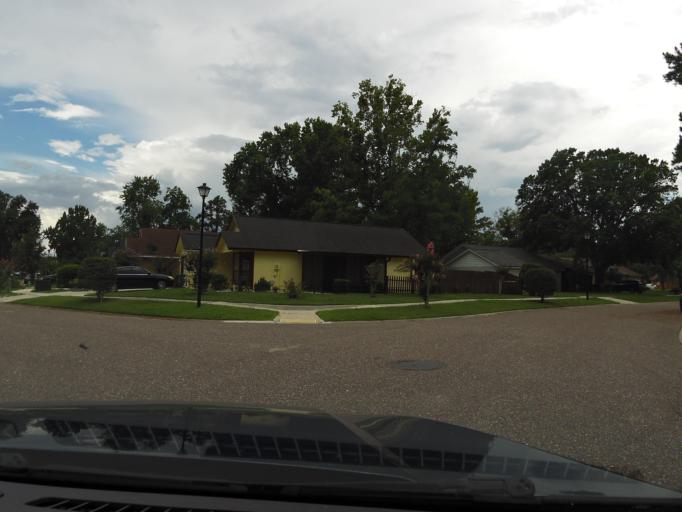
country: US
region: Florida
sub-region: Duval County
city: Jacksonville
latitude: 30.4304
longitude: -81.7002
